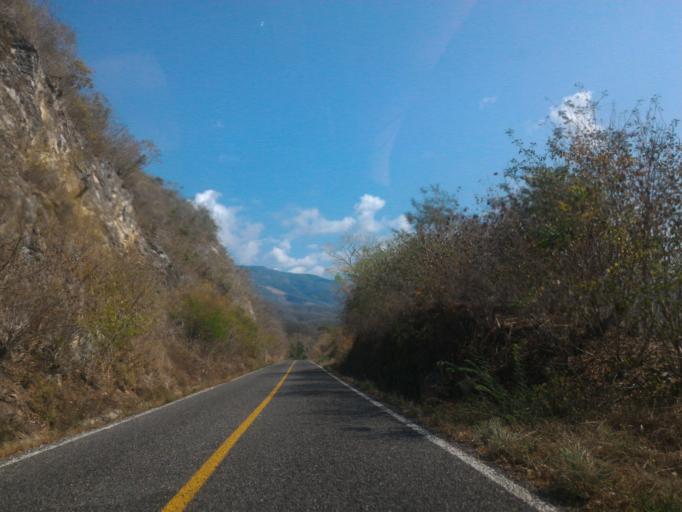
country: MX
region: Michoacan
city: Coahuayana Viejo
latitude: 18.4657
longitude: -103.5498
